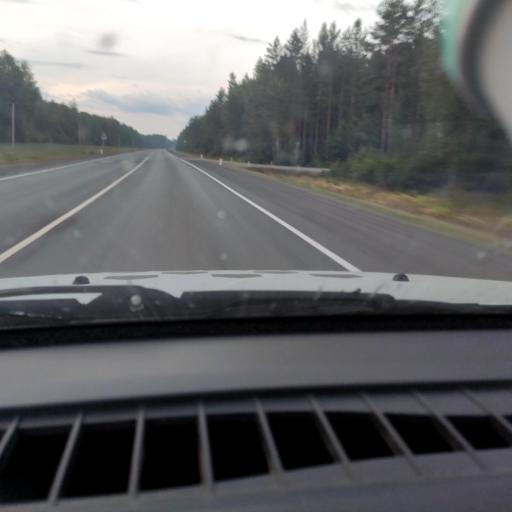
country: RU
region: Kirov
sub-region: Kirovo-Chepetskiy Rayon
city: Kirov
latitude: 58.6905
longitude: 49.6251
